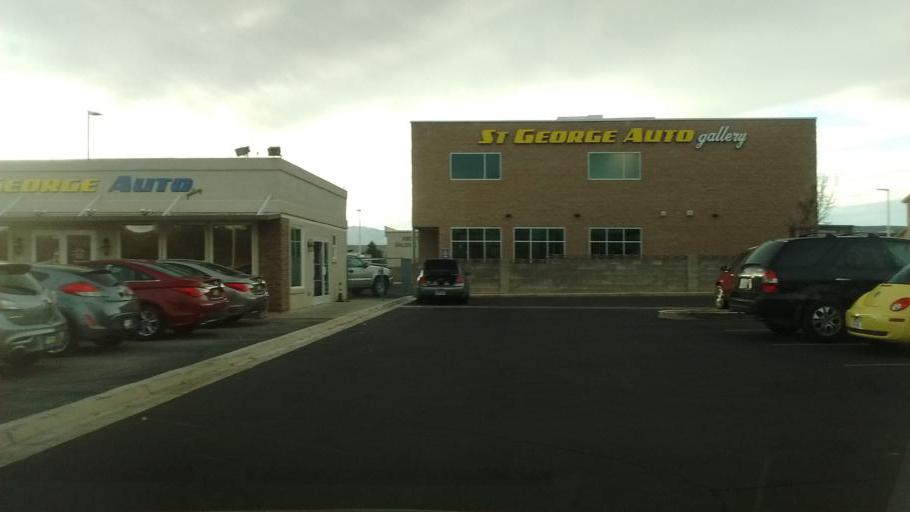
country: US
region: Utah
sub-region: Washington County
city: Saint George
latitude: 37.0968
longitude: -113.5603
